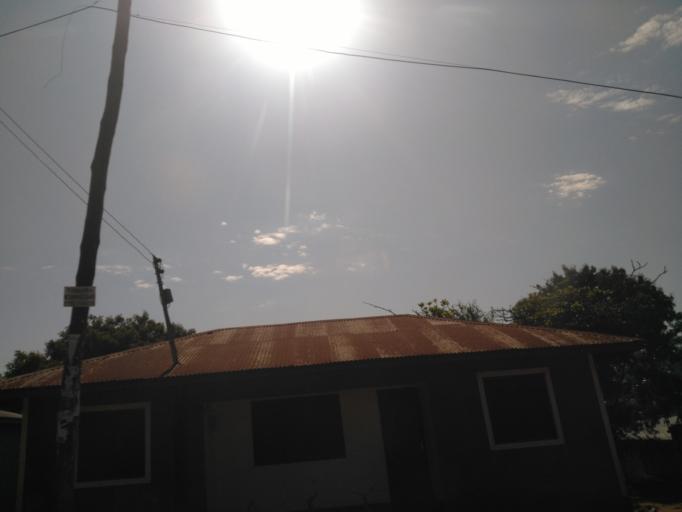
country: TZ
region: Mwanza
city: Mwanza
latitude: -2.4961
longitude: 32.8976
